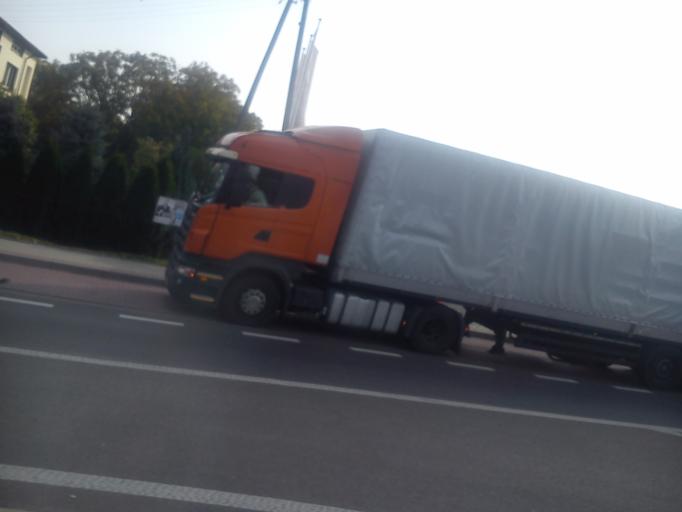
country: PL
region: Subcarpathian Voivodeship
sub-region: Powiat lancucki
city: Lancut
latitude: 50.0582
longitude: 22.2098
